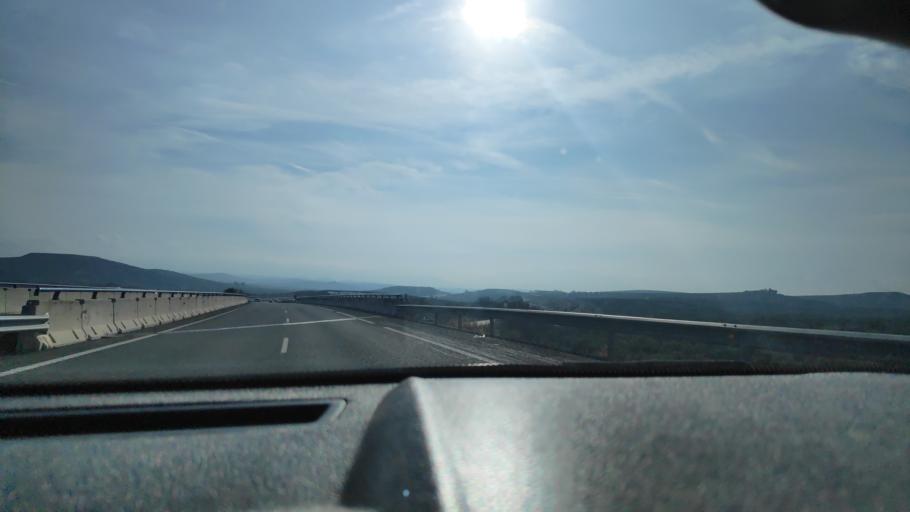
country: ES
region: Andalusia
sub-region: Provincia de Jaen
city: Mengibar
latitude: 37.8862
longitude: -3.7763
